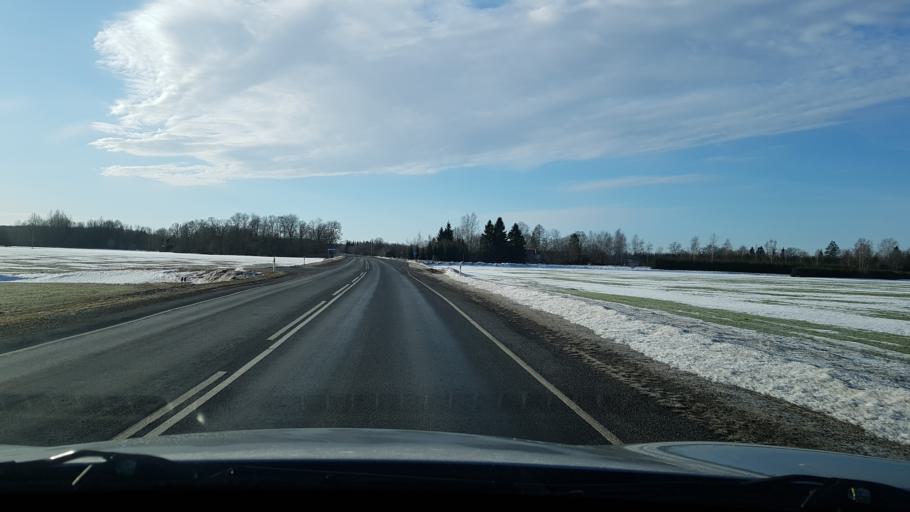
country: EE
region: Viljandimaa
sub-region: Vohma linn
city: Vohma
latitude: 58.6431
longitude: 25.5788
